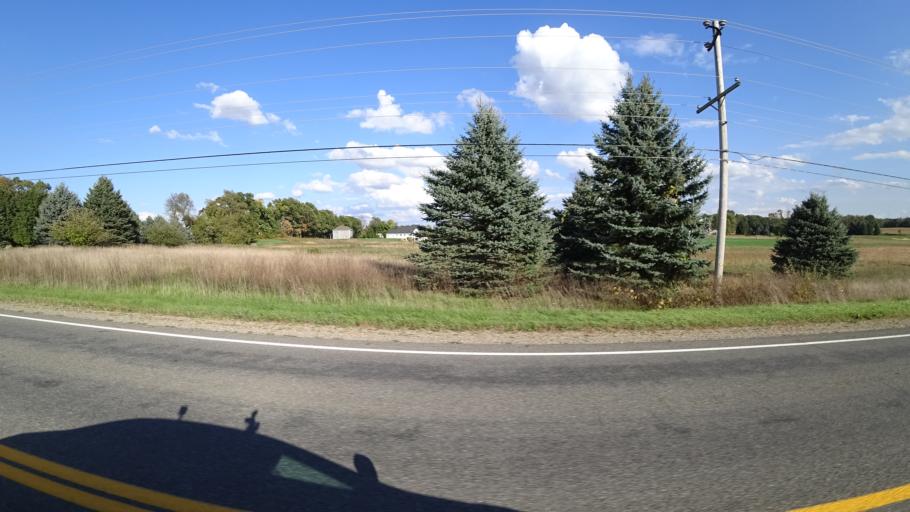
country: US
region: Michigan
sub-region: Saint Joseph County
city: Centreville
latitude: 41.9000
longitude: -85.5070
